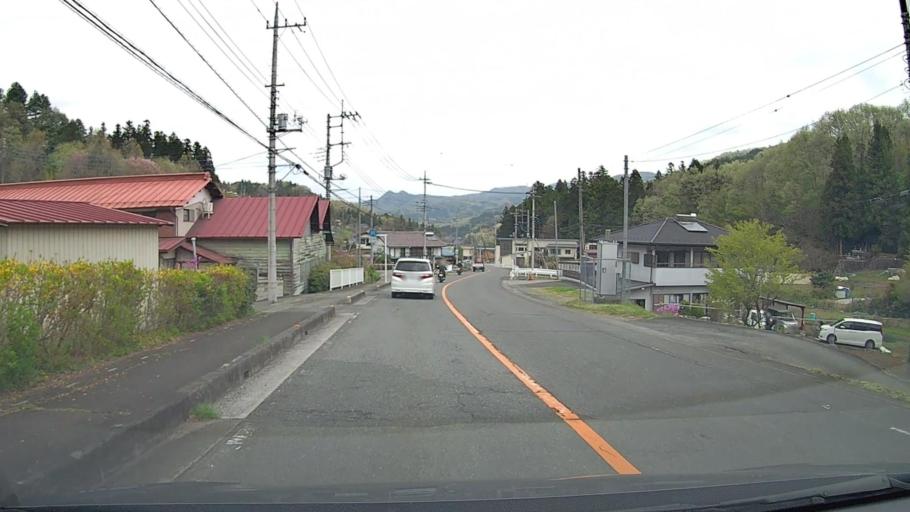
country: JP
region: Saitama
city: Chichibu
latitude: 36.0380
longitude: 139.1283
